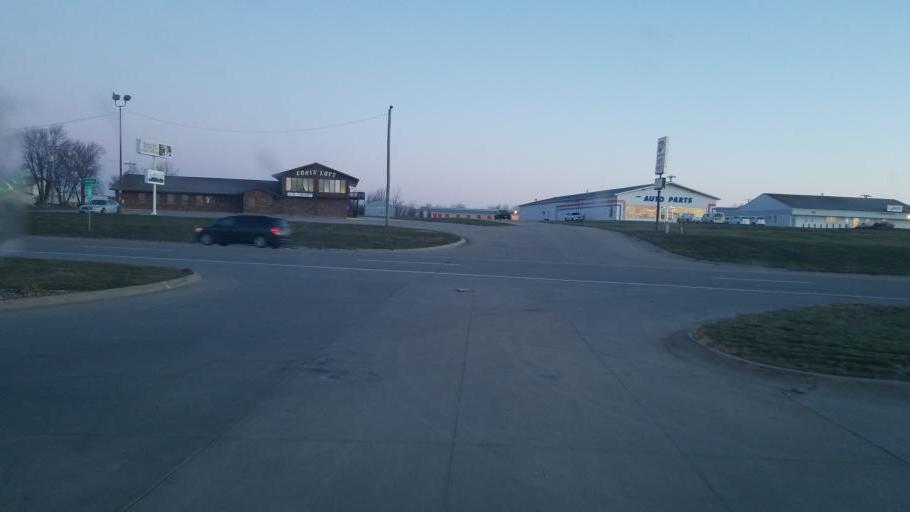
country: US
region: Iowa
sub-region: Henry County
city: Mount Pleasant
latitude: 40.9603
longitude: -91.5236
